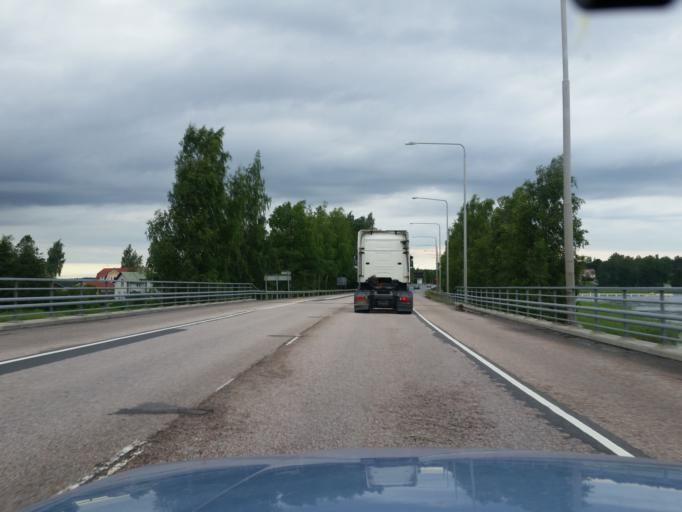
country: FI
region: Uusimaa
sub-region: Raaseporin
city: Ekenaes
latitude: 59.9823
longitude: 23.4353
